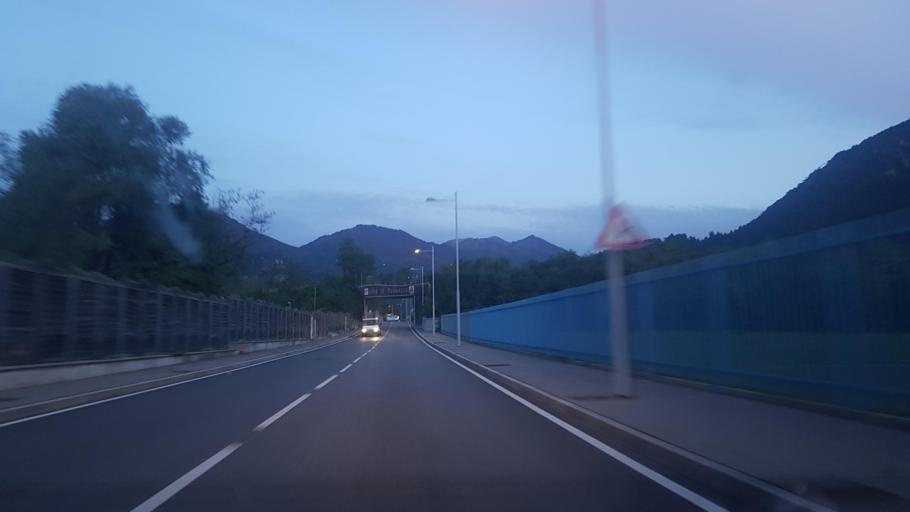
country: IT
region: Friuli Venezia Giulia
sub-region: Provincia di Udine
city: Tolmezzo
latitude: 46.3917
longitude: 13.0248
